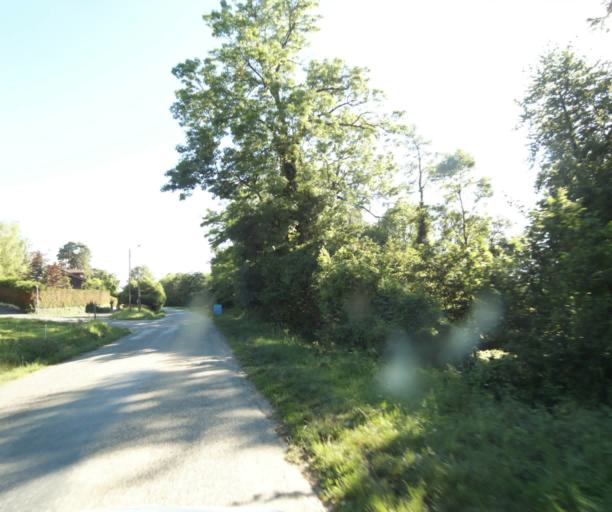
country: FR
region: Rhone-Alpes
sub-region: Departement de la Haute-Savoie
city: Ballaison
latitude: 46.3031
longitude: 6.3315
